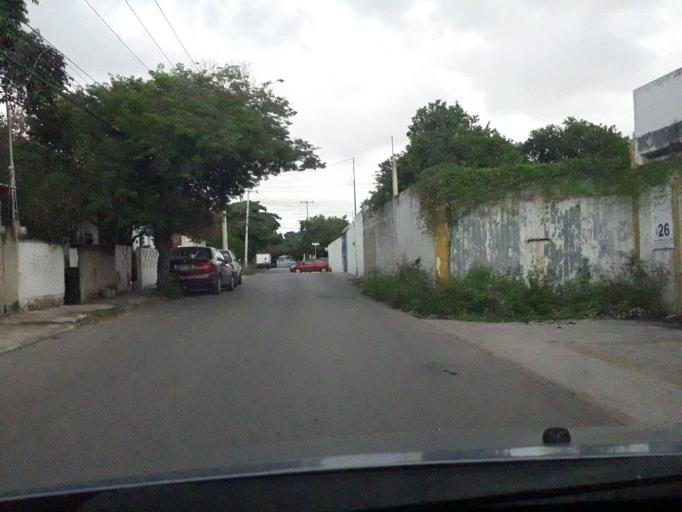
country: MX
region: Yucatan
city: Merida
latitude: 21.0192
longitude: -89.6341
